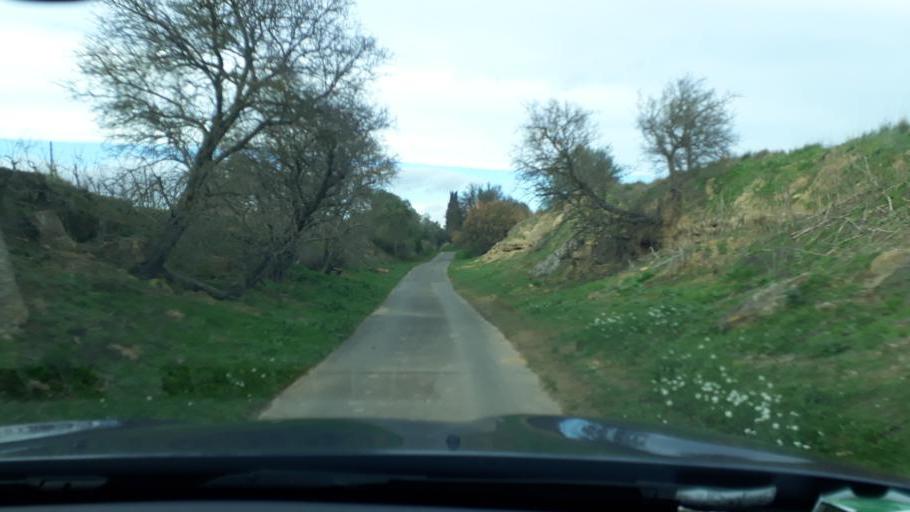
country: FR
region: Languedoc-Roussillon
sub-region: Departement de l'Herault
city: Florensac
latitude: 43.4073
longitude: 3.4600
